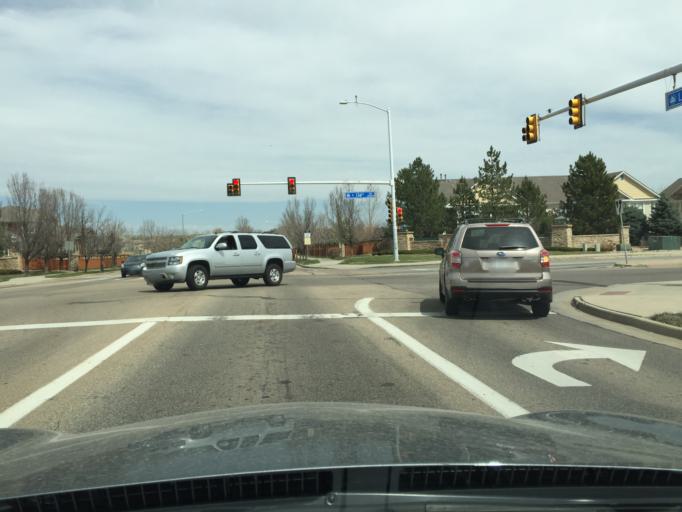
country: US
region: Colorado
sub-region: Broomfield County
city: Broomfield
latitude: 39.9429
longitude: -105.0344
